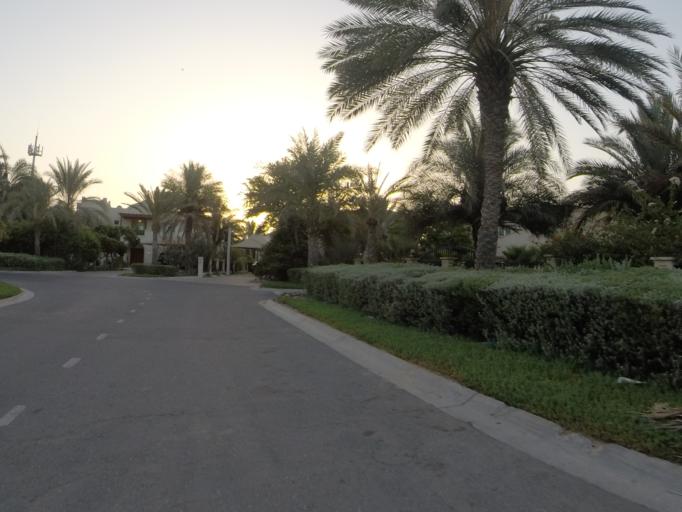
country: AE
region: Dubai
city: Dubai
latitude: 25.0572
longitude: 55.1613
